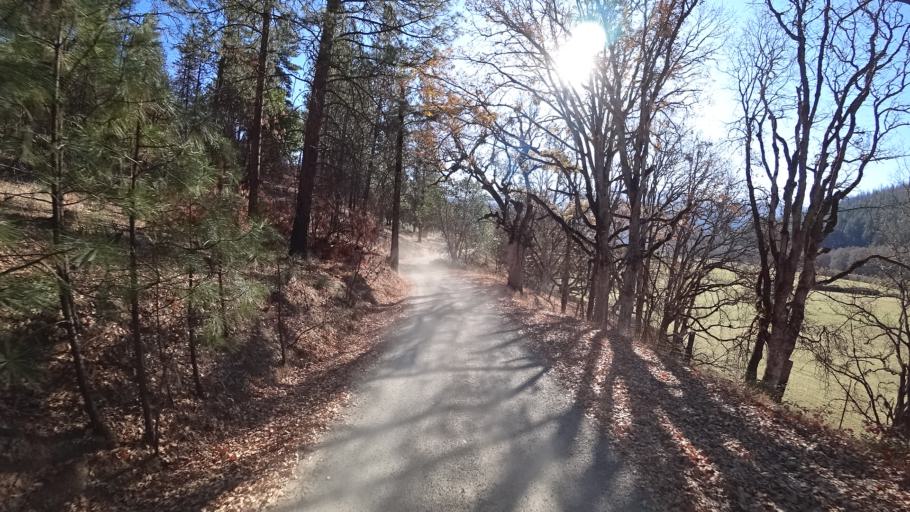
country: US
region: California
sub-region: Siskiyou County
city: Happy Camp
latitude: 41.8391
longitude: -123.0107
